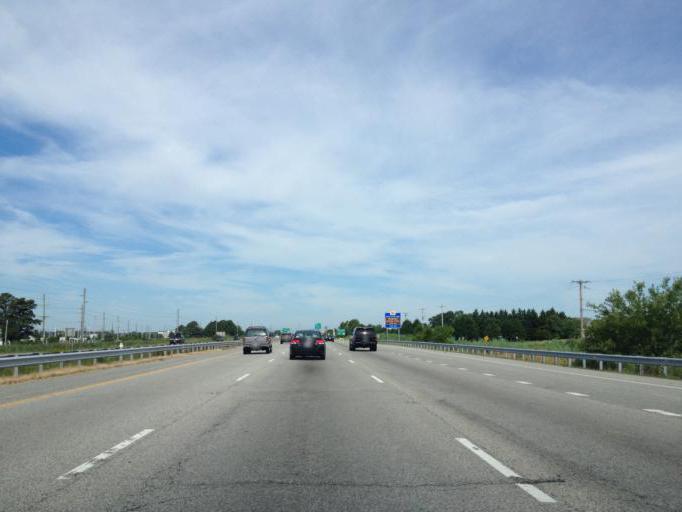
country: US
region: Maryland
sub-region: Queen Anne's County
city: Grasonville
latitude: 38.9655
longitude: -76.2238
